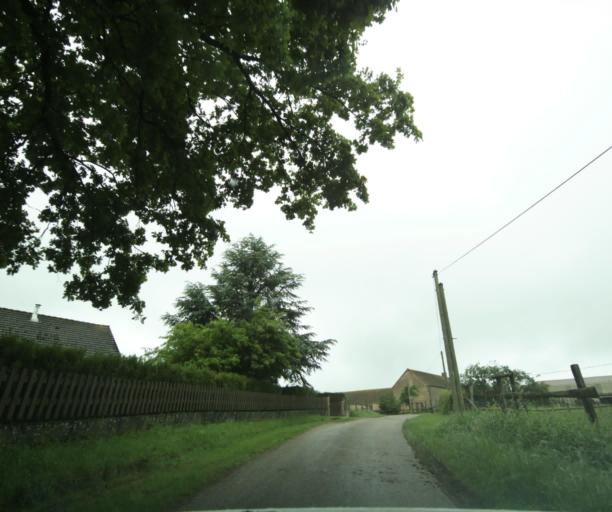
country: FR
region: Bourgogne
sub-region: Departement de Saone-et-Loire
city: Charolles
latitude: 46.4321
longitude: 4.3246
